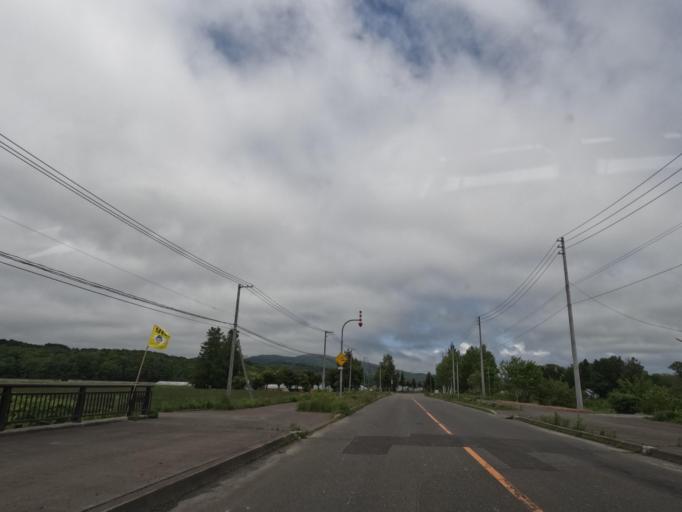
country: JP
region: Hokkaido
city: Tobetsu
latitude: 43.2571
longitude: 141.5234
